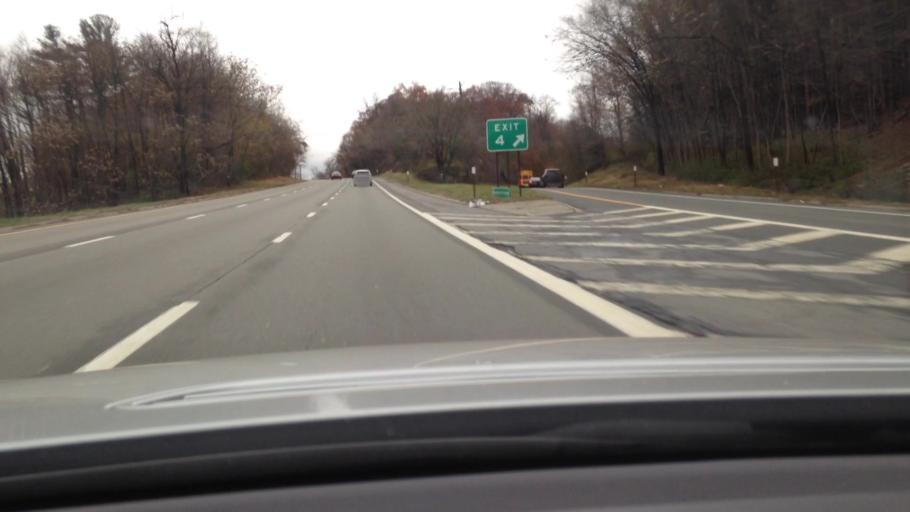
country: US
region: New York
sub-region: Westchester County
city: Hawthorne
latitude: 41.1192
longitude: -73.8068
